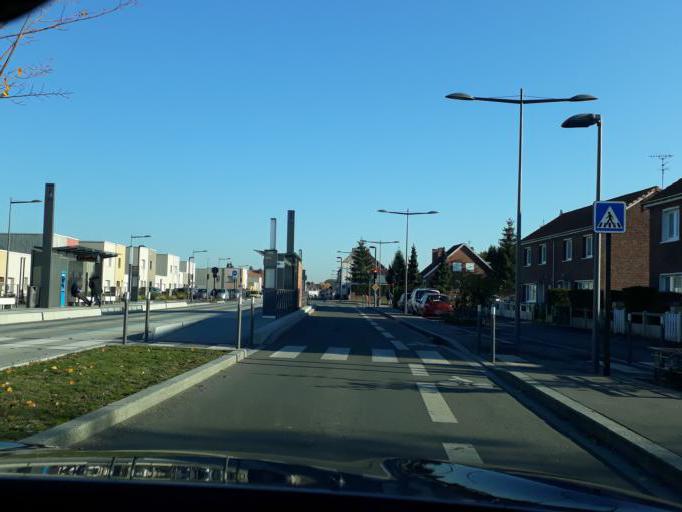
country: FR
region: Nord-Pas-de-Calais
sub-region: Departement du Nord
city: Auberchicourt
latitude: 50.3345
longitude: 3.2215
